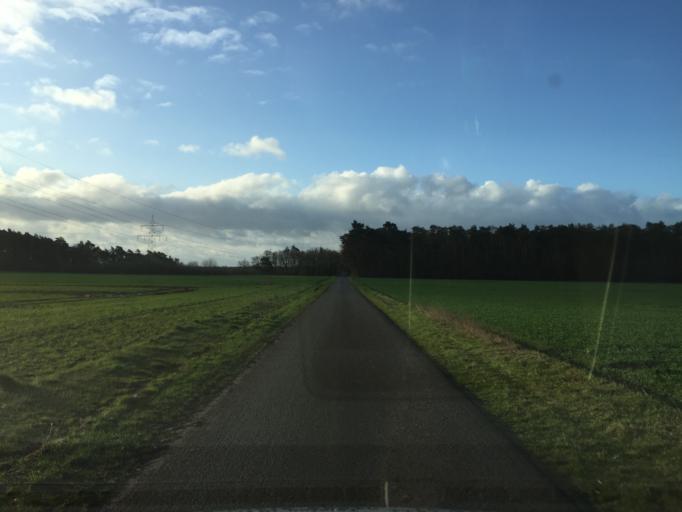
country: DE
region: Lower Saxony
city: Steyerberg
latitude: 52.6025
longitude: 8.9876
